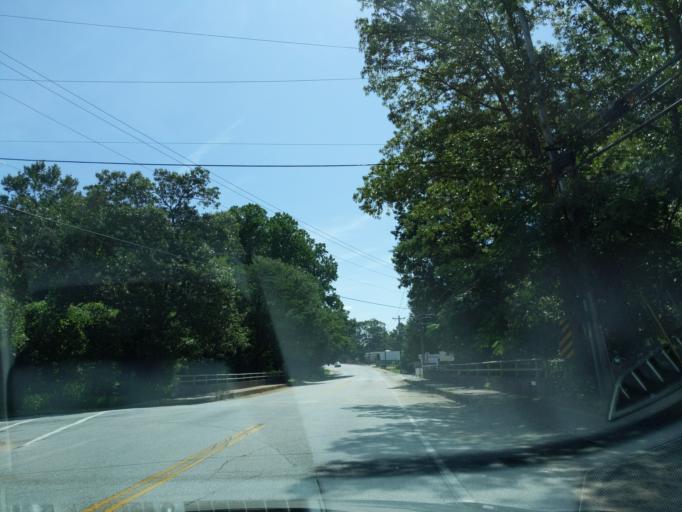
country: US
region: South Carolina
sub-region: Greenville County
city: Taylors
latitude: 34.9195
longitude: -82.3065
